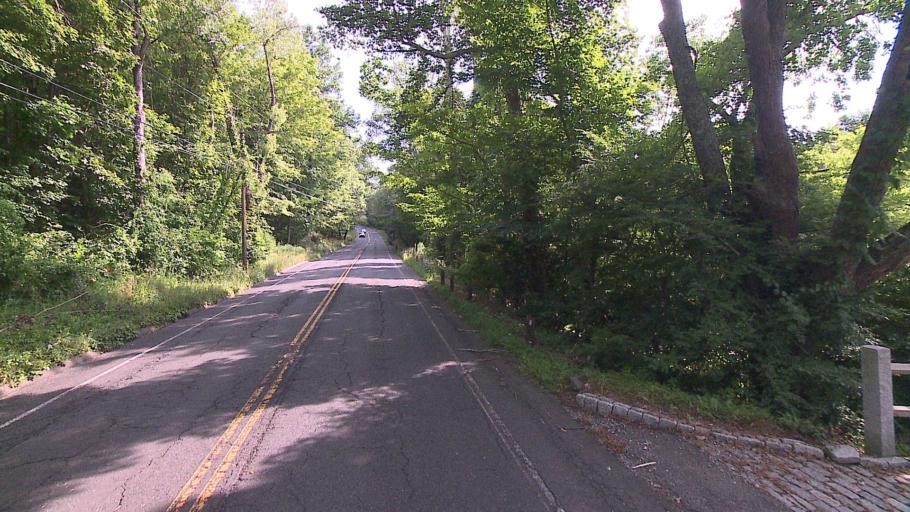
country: US
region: New York
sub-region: Putnam County
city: Putnam Lake
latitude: 41.5178
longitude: -73.5207
